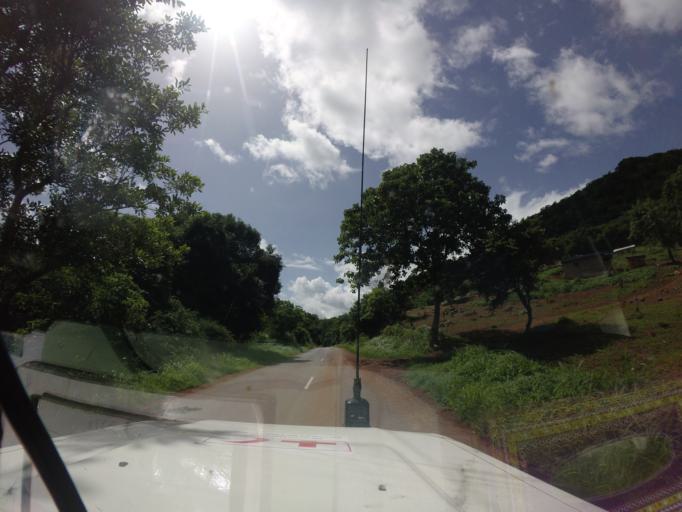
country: GN
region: Mamou
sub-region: Mamou Prefecture
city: Mamou
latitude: 10.2462
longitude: -11.8814
